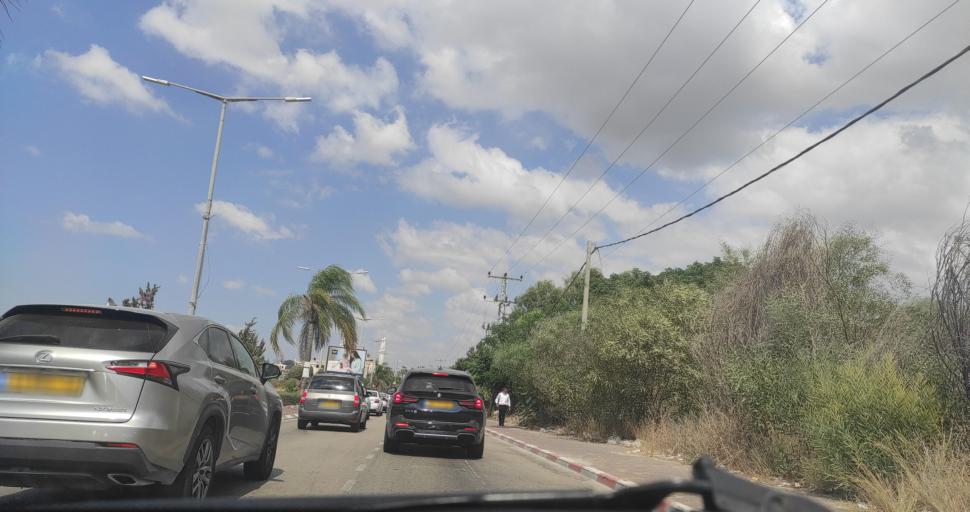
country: IL
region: Central District
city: Kafr Qasim
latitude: 32.1097
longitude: 34.9633
